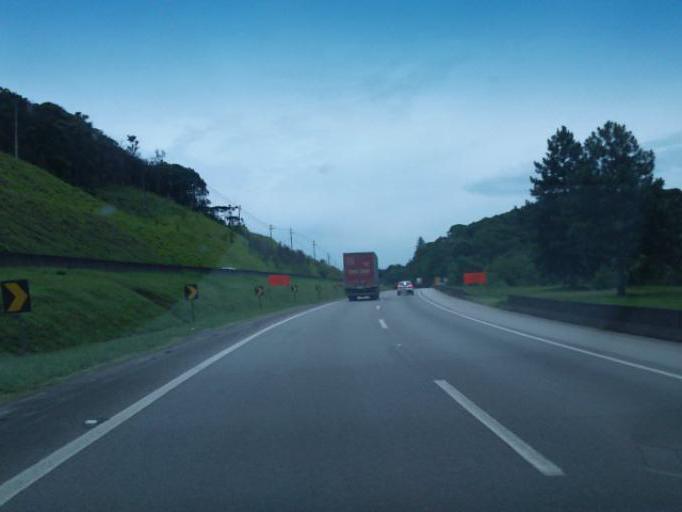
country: BR
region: Sao Paulo
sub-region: Juquitiba
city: Juquitiba
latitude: -23.9402
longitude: -47.0429
